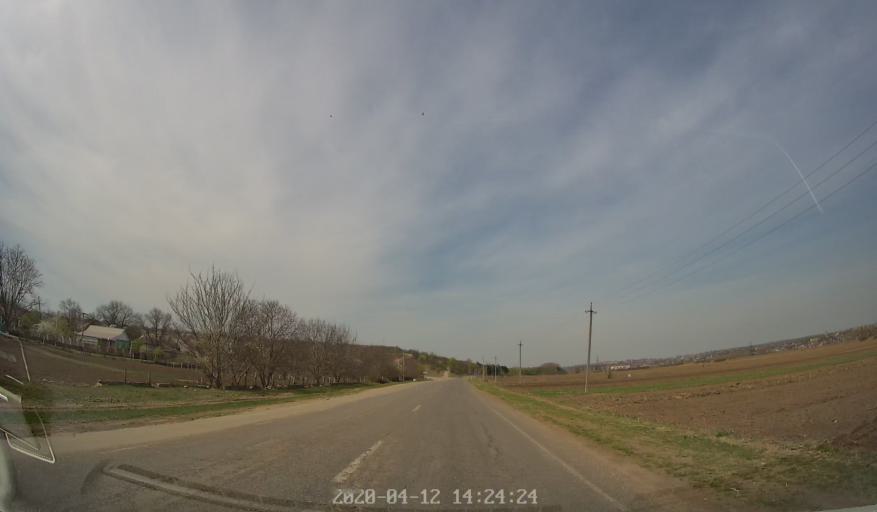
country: MD
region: Telenesti
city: Dubasari
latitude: 47.2619
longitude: 29.1294
